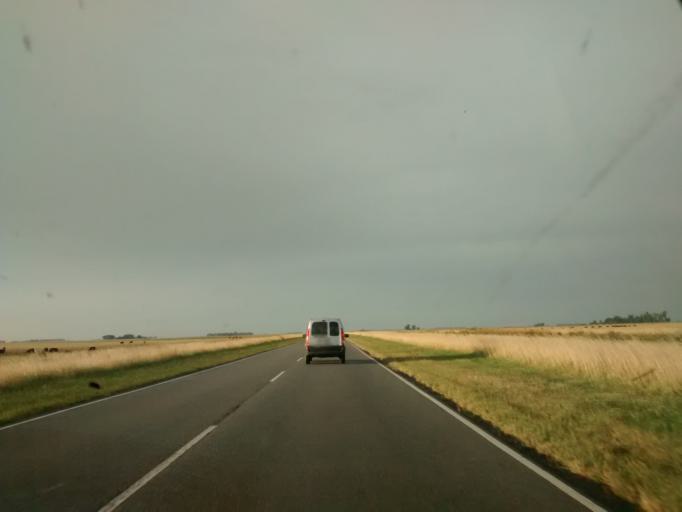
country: AR
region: Buenos Aires
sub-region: Partido de General Belgrano
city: General Belgrano
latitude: -36.2770
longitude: -58.5859
